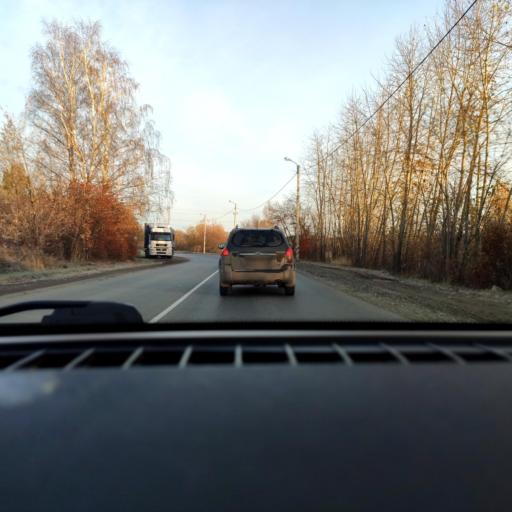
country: RU
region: Perm
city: Kondratovo
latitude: 57.9439
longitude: 56.1531
